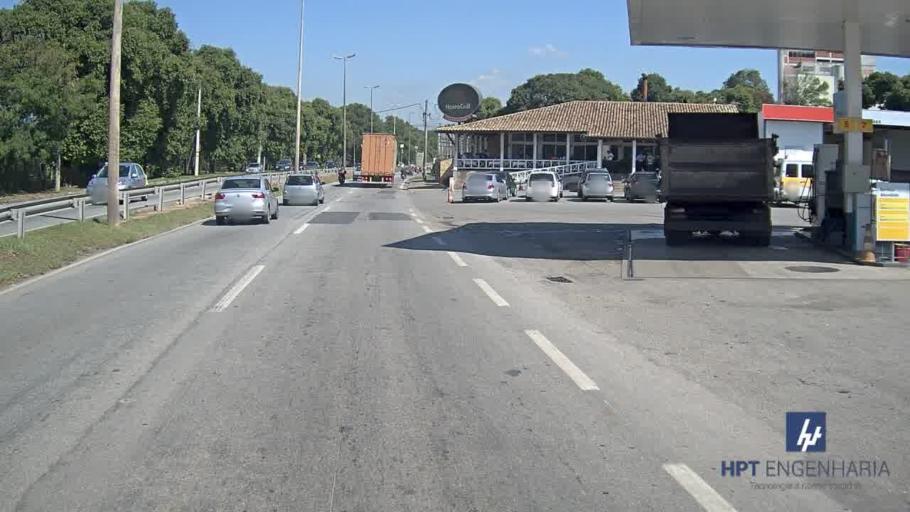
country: BR
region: Minas Gerais
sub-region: Ipatinga
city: Ipatinga
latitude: -19.5029
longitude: -42.5679
